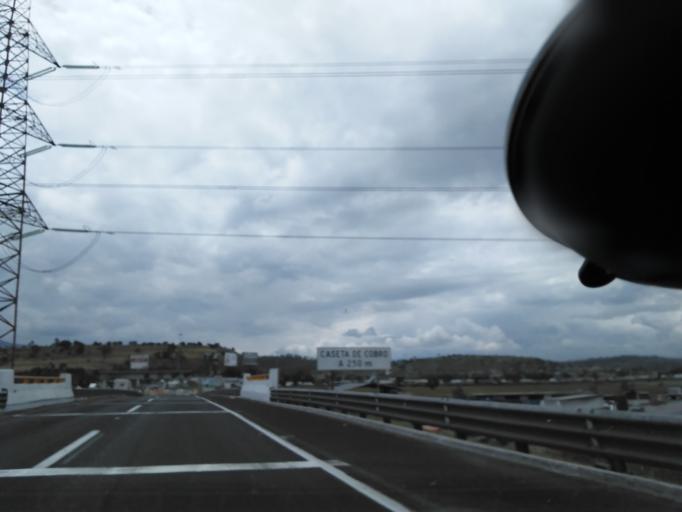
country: MX
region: Mexico
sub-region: Huehuetoca
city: Jorobas
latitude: 19.8215
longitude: -99.2376
